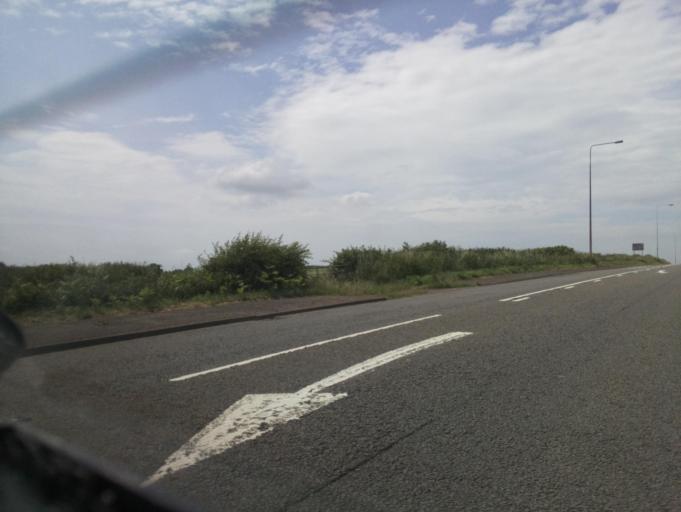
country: GB
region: Wales
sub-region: Vale of Glamorgan
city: Llangan
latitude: 51.4771
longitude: -3.5138
